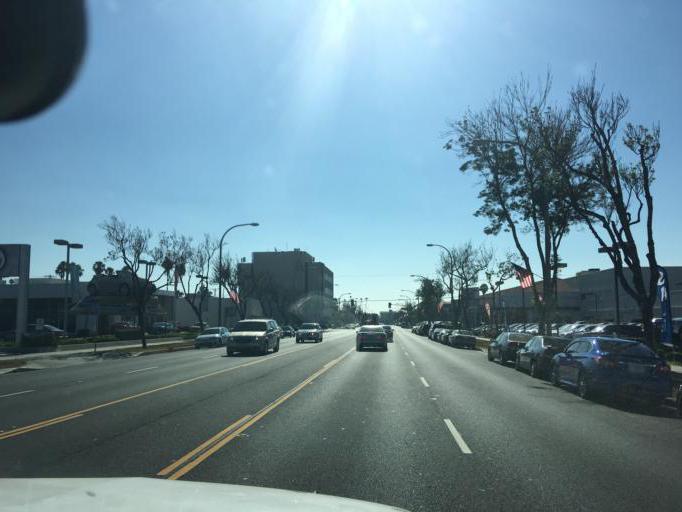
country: US
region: California
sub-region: Los Angeles County
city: Alhambra
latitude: 34.0915
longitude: -118.1436
